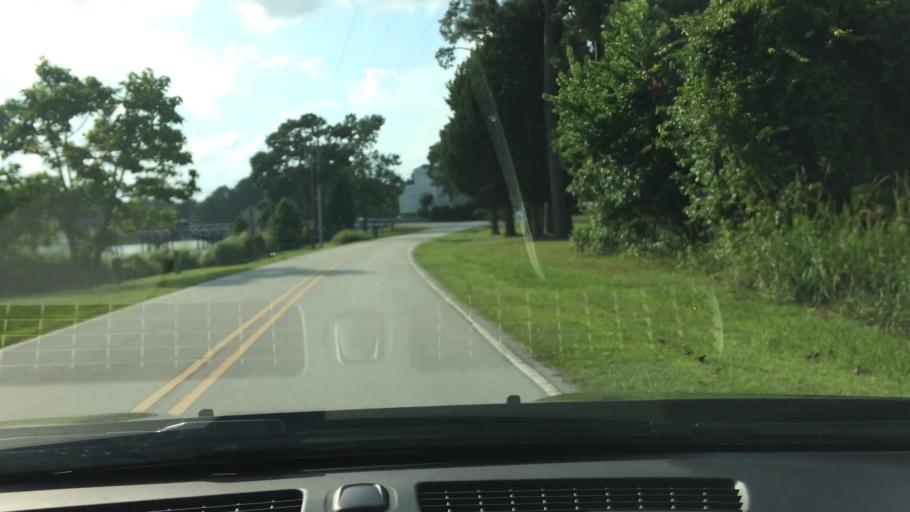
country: US
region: North Carolina
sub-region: Beaufort County
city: River Road
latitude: 35.4328
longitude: -76.9690
